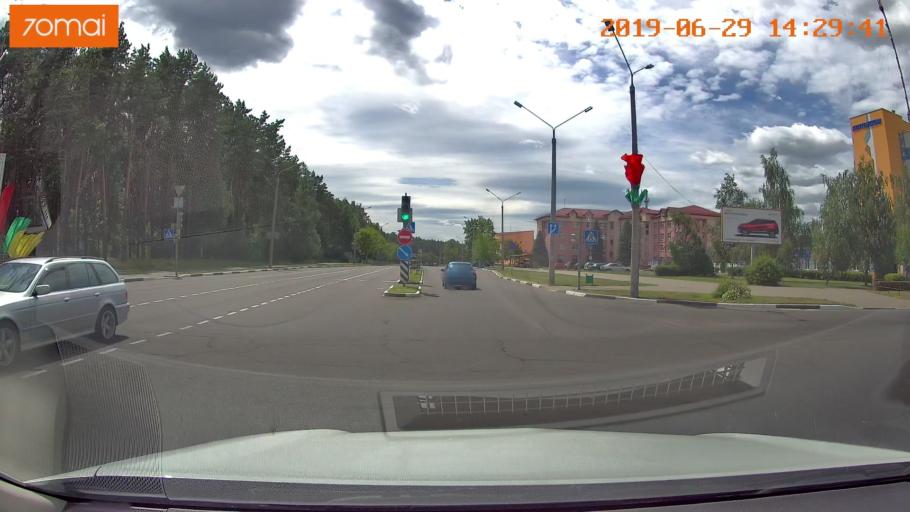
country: BY
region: Minsk
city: Salihorsk
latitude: 52.7829
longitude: 27.5272
